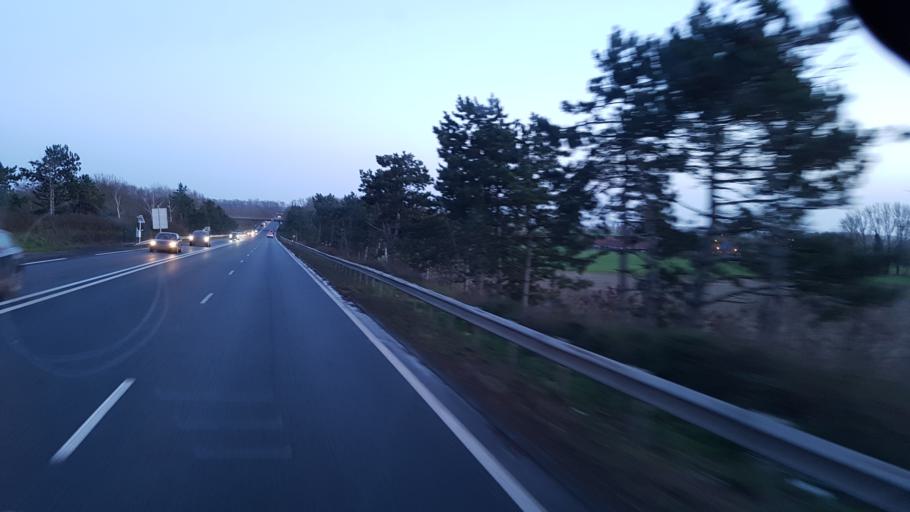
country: FR
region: Nord-Pas-de-Calais
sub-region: Departement du Nord
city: Lambres-lez-Douai
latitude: 50.3478
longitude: 3.0670
